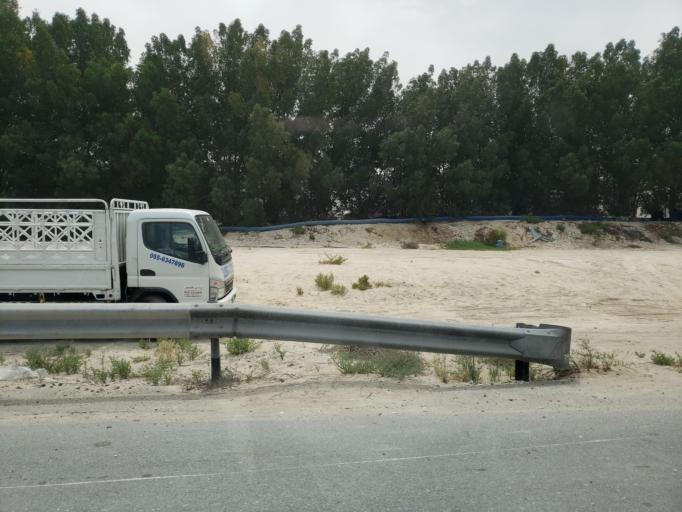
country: AE
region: Dubai
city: Dubai
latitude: 25.0643
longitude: 55.2000
